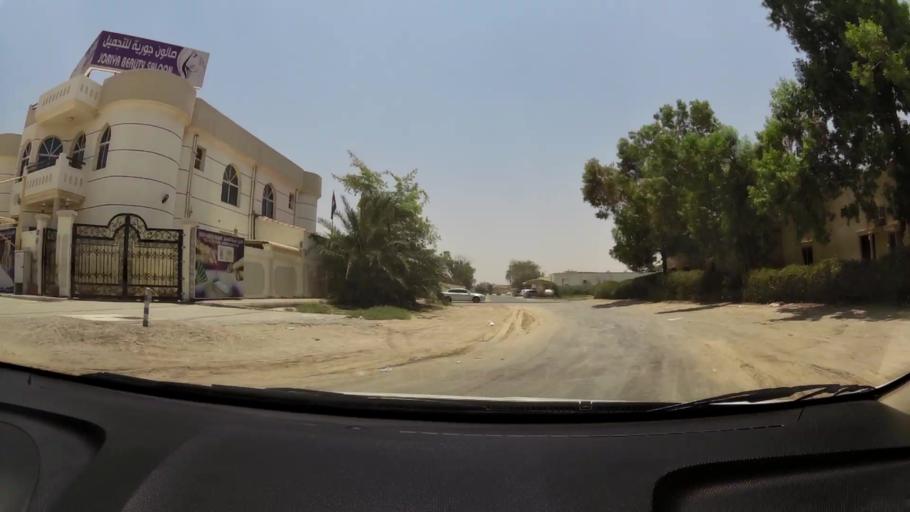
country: AE
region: Umm al Qaywayn
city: Umm al Qaywayn
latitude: 25.5495
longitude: 55.5470
